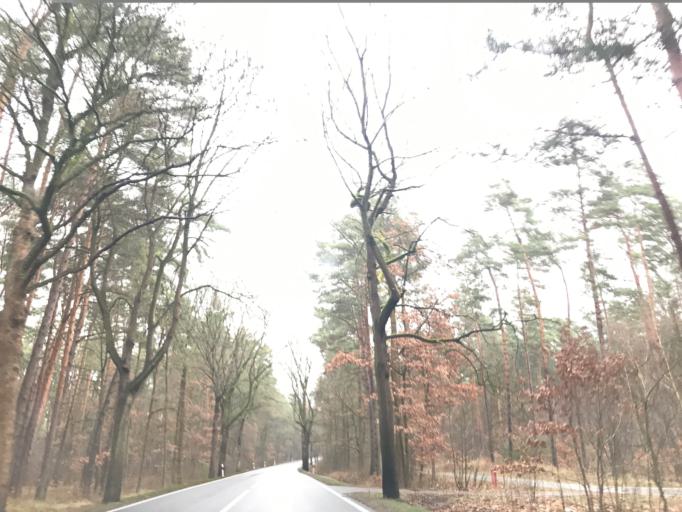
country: DE
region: Brandenburg
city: Kremmen
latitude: 52.6952
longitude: 12.9489
